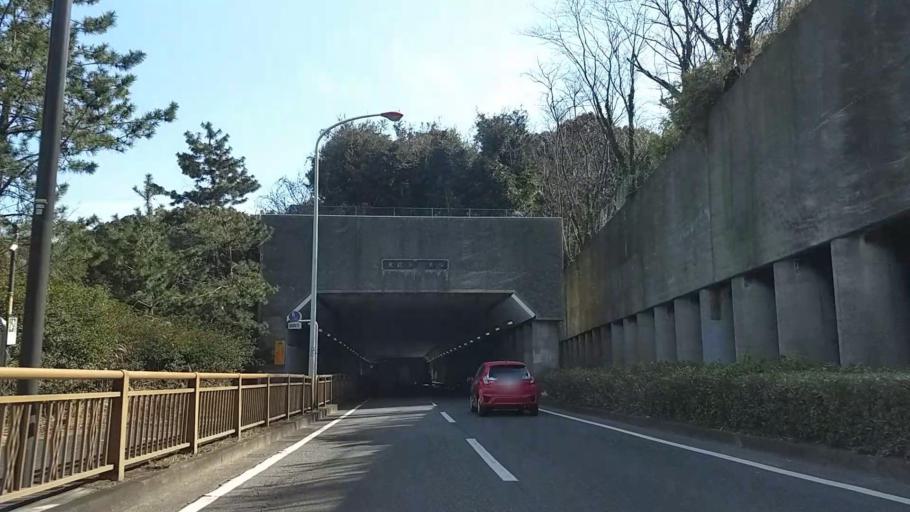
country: JP
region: Kanagawa
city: Fujisawa
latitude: 35.3523
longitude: 139.4445
